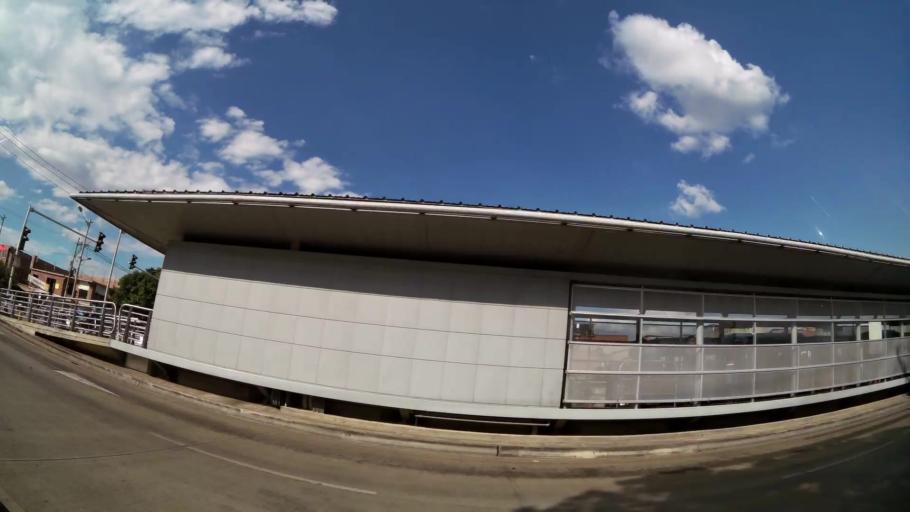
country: CO
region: Valle del Cauca
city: Cali
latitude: 3.4219
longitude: -76.4909
